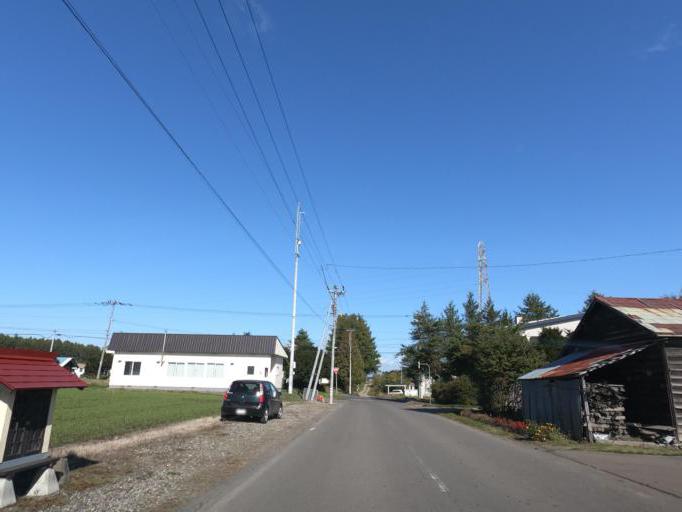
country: JP
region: Hokkaido
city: Otofuke
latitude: 42.9589
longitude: 143.2346
